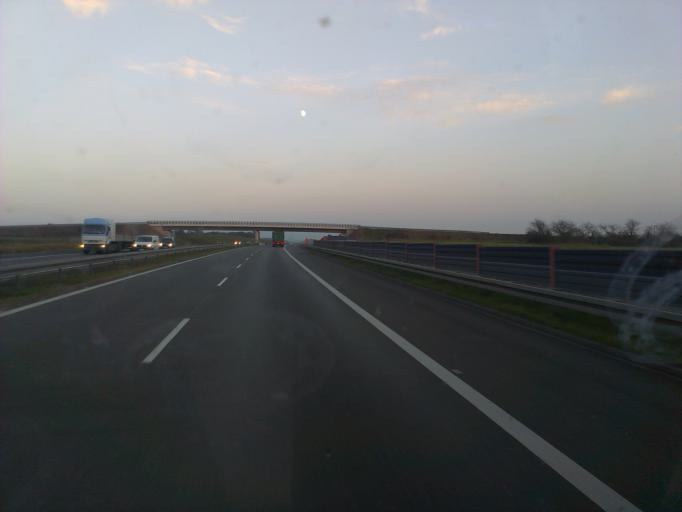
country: PL
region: Opole Voivodeship
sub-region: Powiat krapkowicki
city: Gogolin
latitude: 50.4829
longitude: 18.0481
